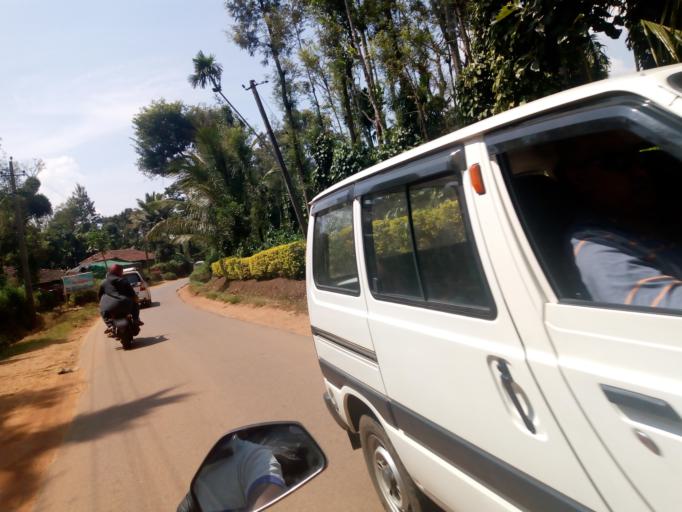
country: IN
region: Karnataka
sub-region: Kodagu
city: Ponnampet
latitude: 12.0306
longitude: 75.9701
